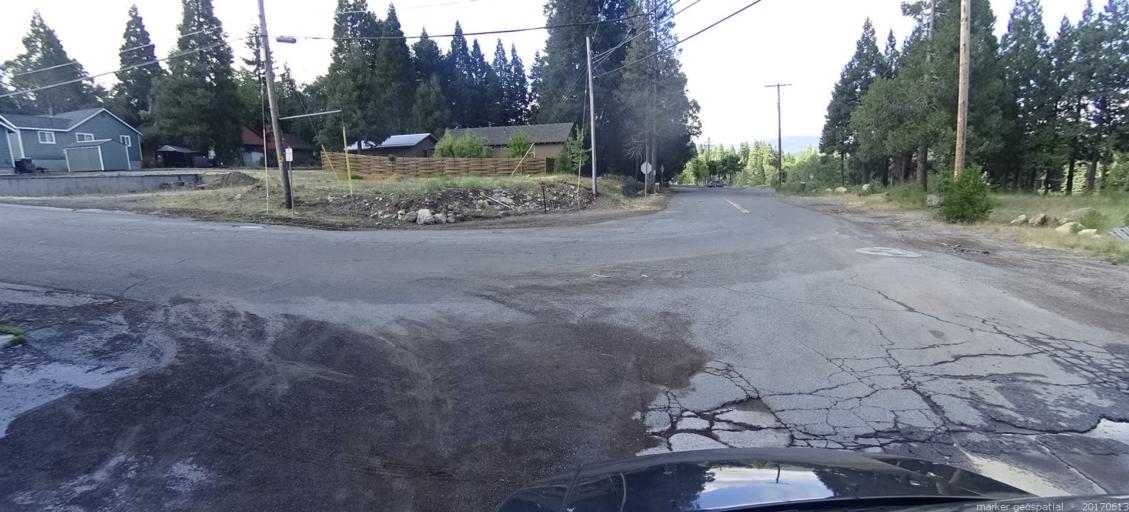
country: US
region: California
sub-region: Siskiyou County
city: Mount Shasta
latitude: 41.3281
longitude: -122.3220
